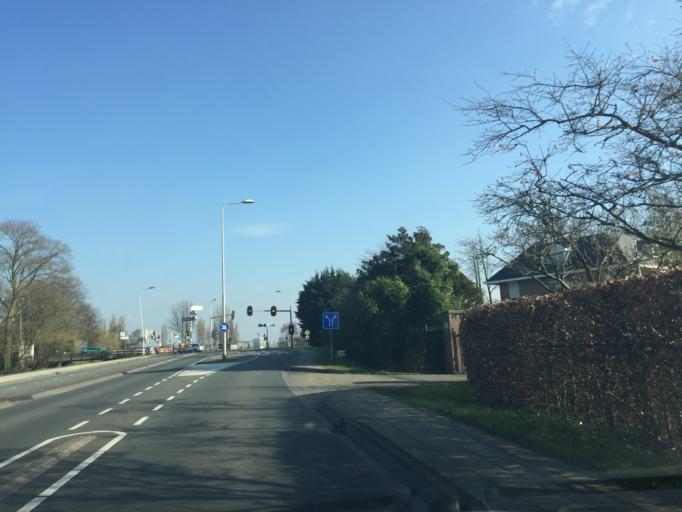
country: NL
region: South Holland
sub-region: Gemeente Oegstgeest
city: Oegstgeest
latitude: 52.1882
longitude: 4.4885
